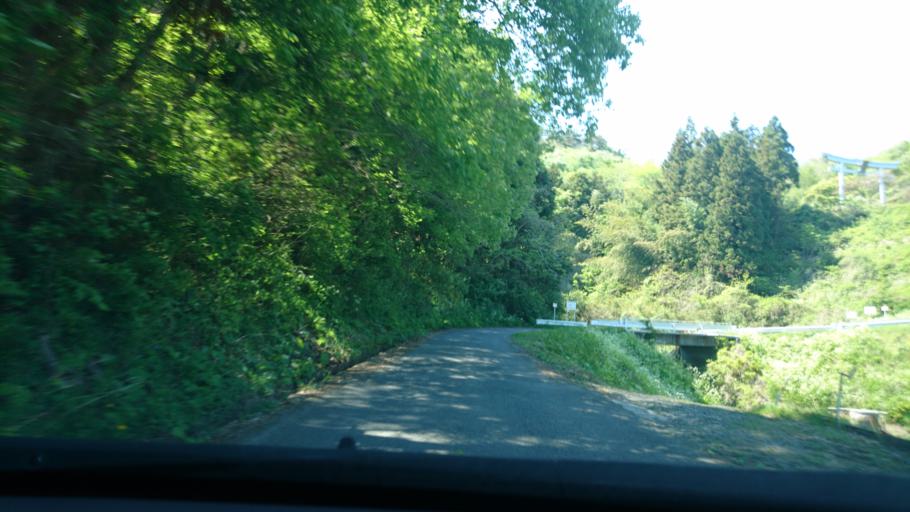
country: JP
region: Iwate
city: Ichinoseki
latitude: 38.9374
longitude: 141.2388
